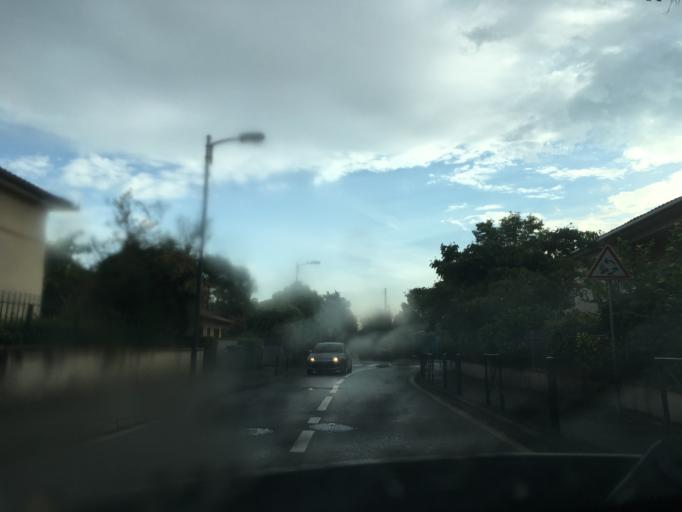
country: FR
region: Midi-Pyrenees
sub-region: Departement de la Haute-Garonne
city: Portet-sur-Garonne
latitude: 43.5610
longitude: 1.3841
